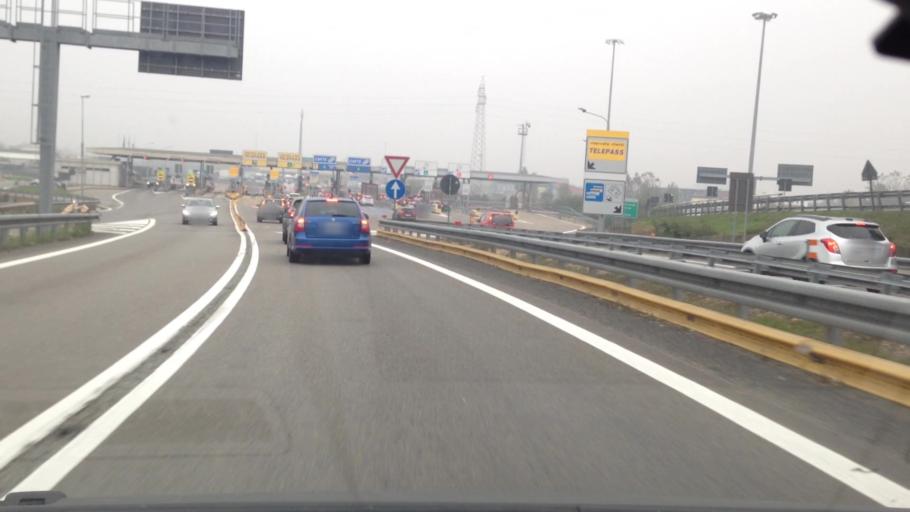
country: IT
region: Piedmont
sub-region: Provincia di Asti
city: Asti
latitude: 44.9082
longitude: 8.2460
